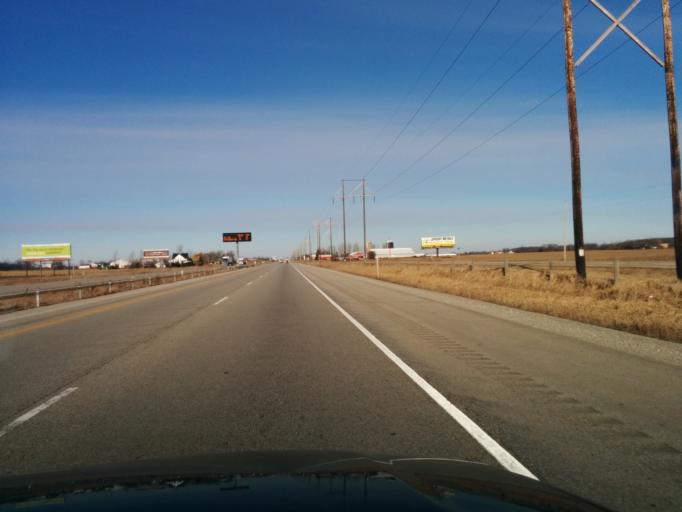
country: US
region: Wisconsin
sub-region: Winnebago County
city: Oshkosh
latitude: 43.9220
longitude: -88.5833
